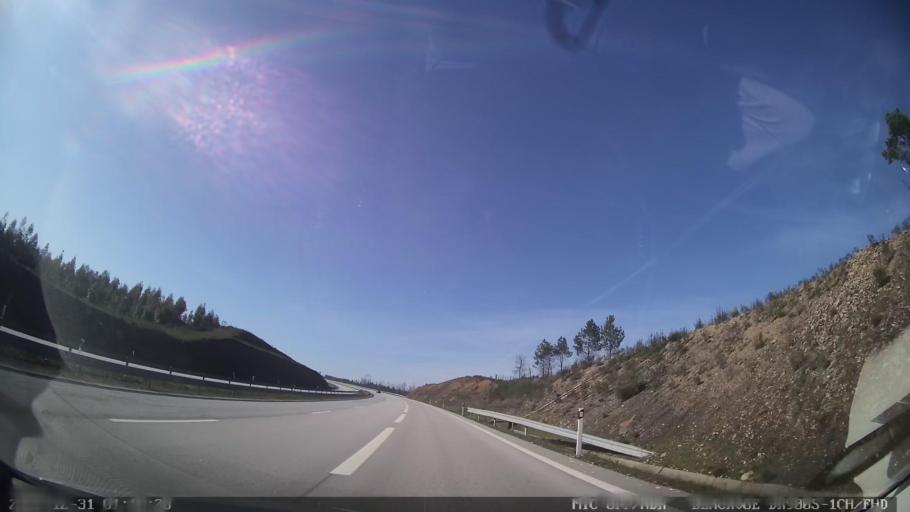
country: PT
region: Portalegre
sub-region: Gaviao
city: Gaviao
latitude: 39.5517
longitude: -7.8397
